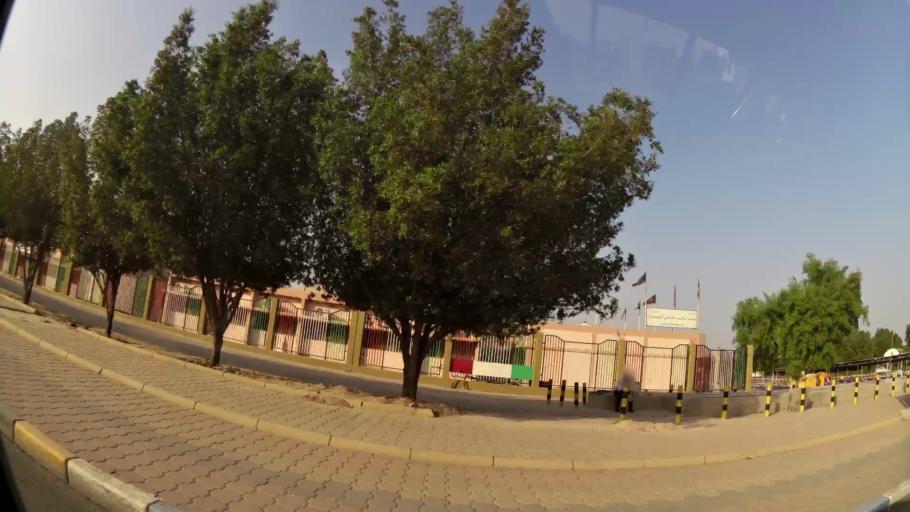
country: KW
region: Muhafazat Hawalli
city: Ar Rumaythiyah
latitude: 29.3157
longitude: 48.0806
